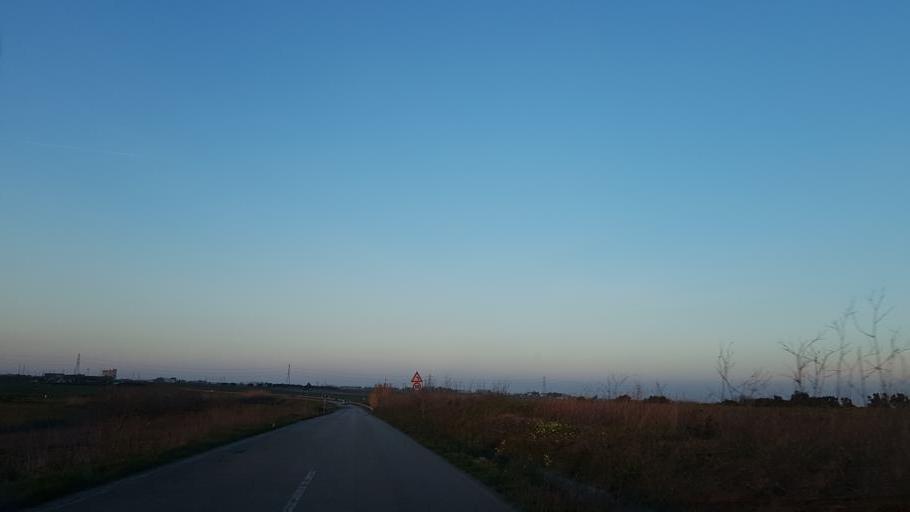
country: IT
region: Apulia
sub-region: Provincia di Brindisi
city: La Rosa
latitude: 40.5769
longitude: 17.9498
